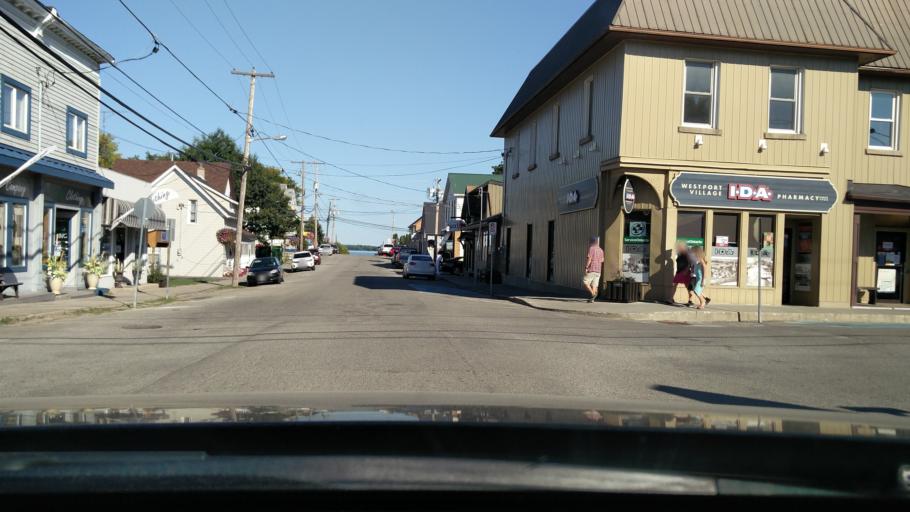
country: CA
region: Ontario
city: Perth
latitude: 44.6796
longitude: -76.3968
